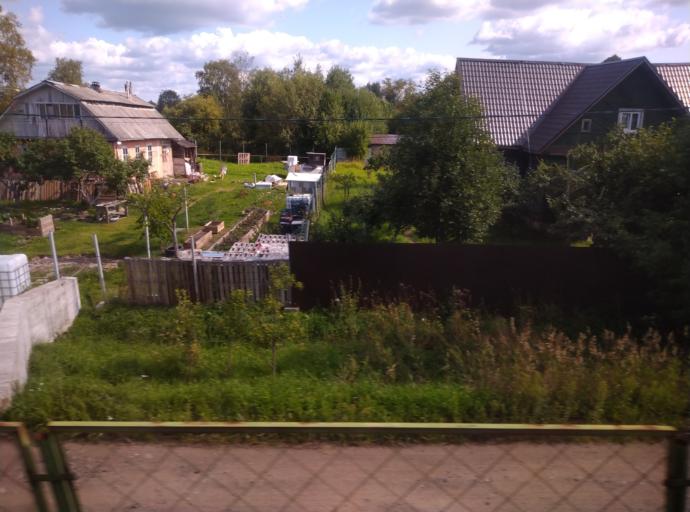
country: RU
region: Leningrad
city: Ul'yanovka
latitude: 59.6410
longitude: 30.7503
